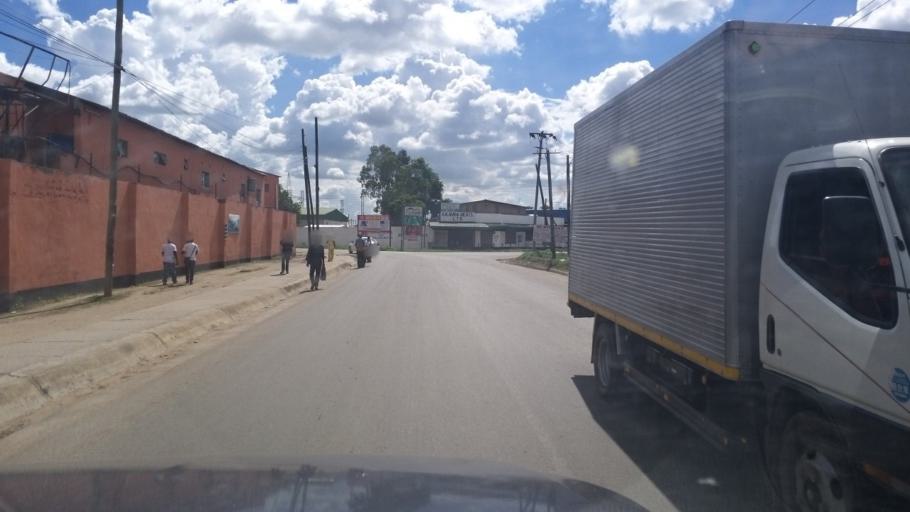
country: ZM
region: Lusaka
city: Lusaka
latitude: -15.4123
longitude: 28.2752
